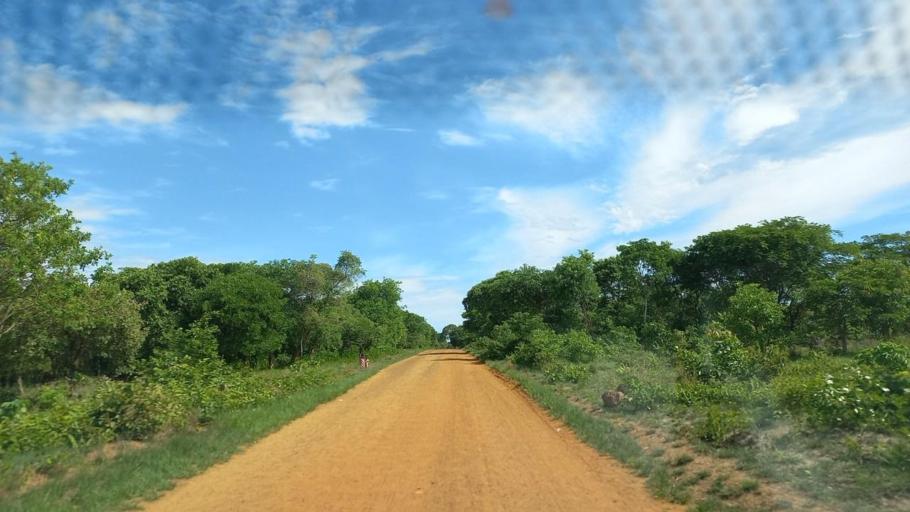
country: ZM
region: North-Western
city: Kabompo
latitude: -13.0662
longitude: 24.2187
